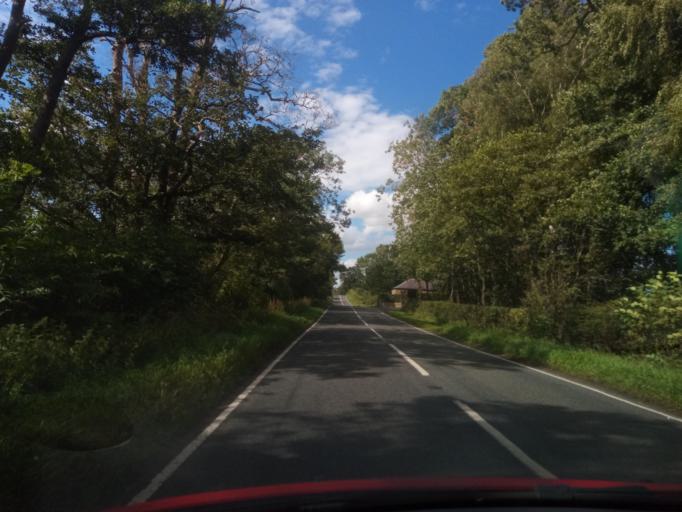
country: GB
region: Scotland
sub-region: The Scottish Borders
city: Coldstream
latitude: 55.6561
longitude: -2.2929
